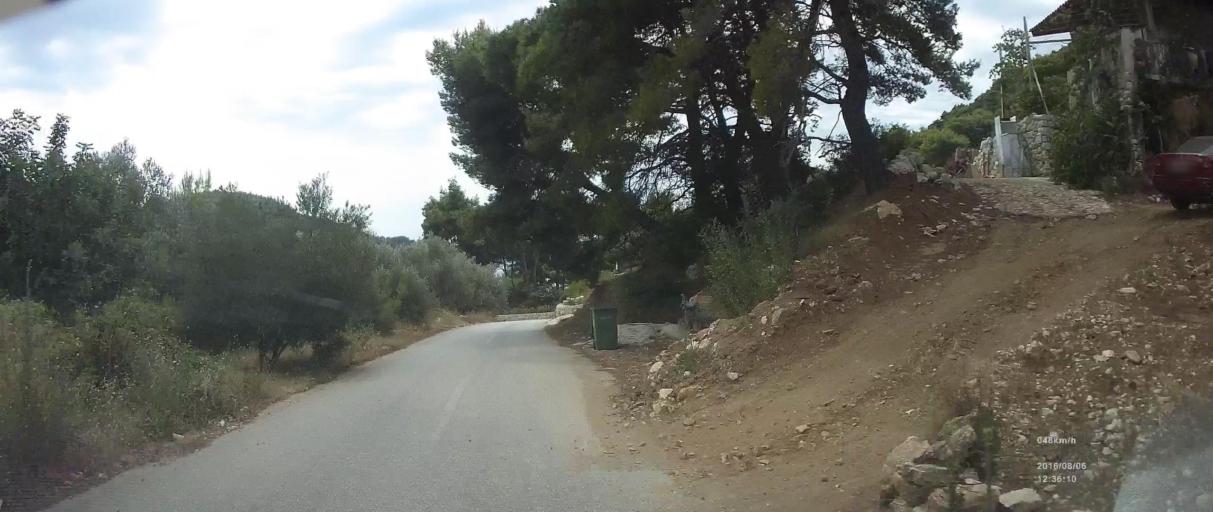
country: HR
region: Dubrovacko-Neretvanska
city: Ston
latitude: 42.7027
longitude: 17.7362
